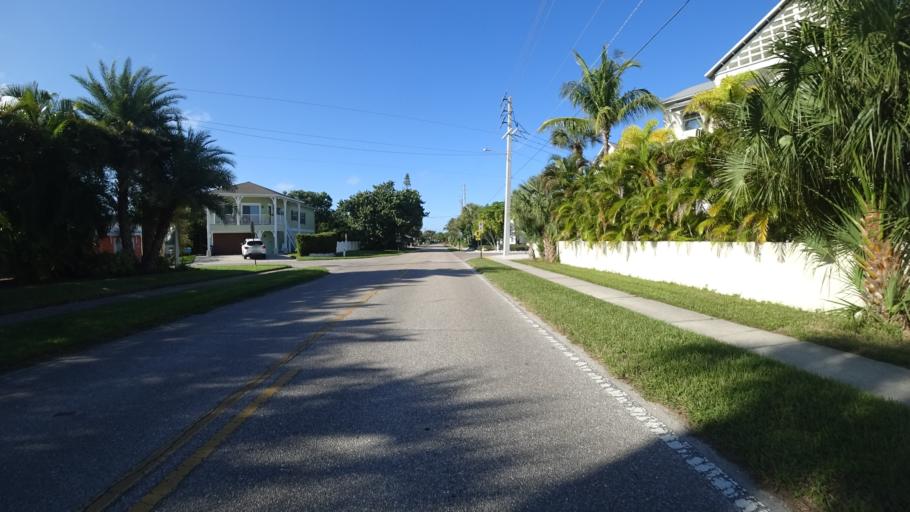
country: US
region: Florida
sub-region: Manatee County
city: Anna Maria
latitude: 27.5181
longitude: -82.7260
